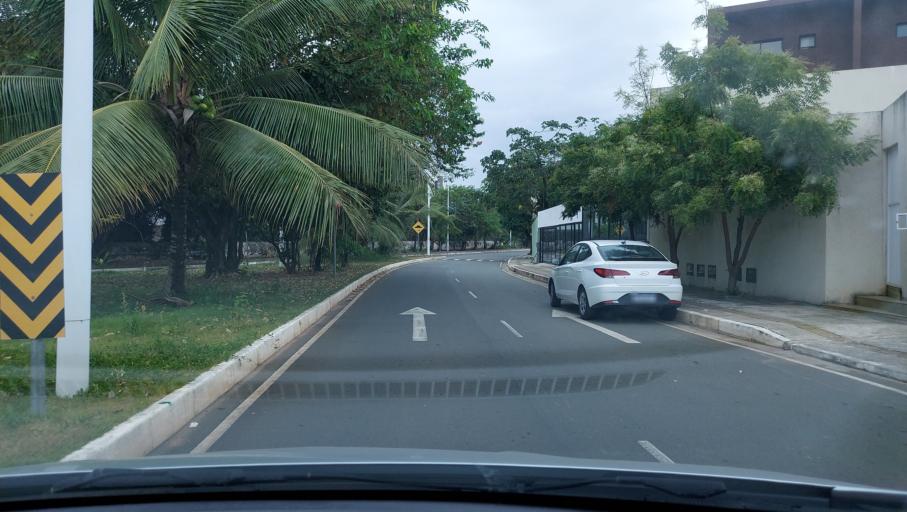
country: BR
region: Bahia
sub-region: Lauro De Freitas
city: Lauro de Freitas
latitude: -12.9526
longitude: -38.3954
